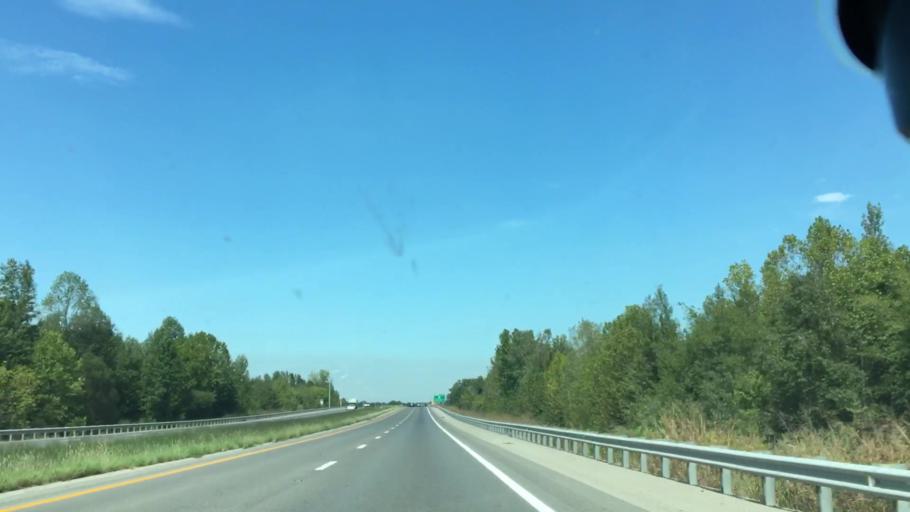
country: US
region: Kentucky
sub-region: Hopkins County
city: Earlington
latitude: 37.2881
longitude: -87.4590
